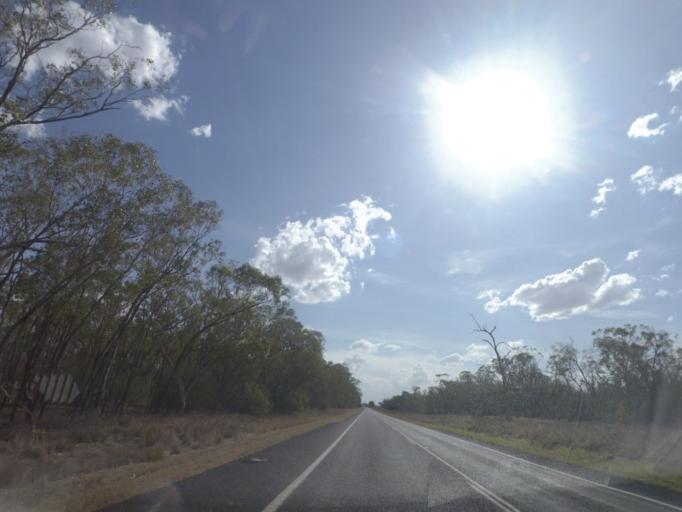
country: AU
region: New South Wales
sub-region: Moree Plains
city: Boggabilla
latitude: -28.5461
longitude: 150.8770
